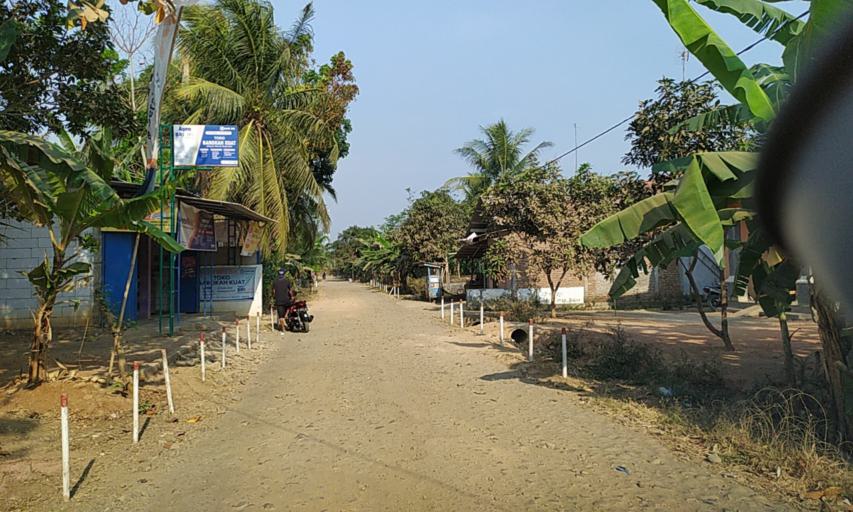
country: ID
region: Central Java
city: Padangsari
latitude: -7.3549
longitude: 108.7550
